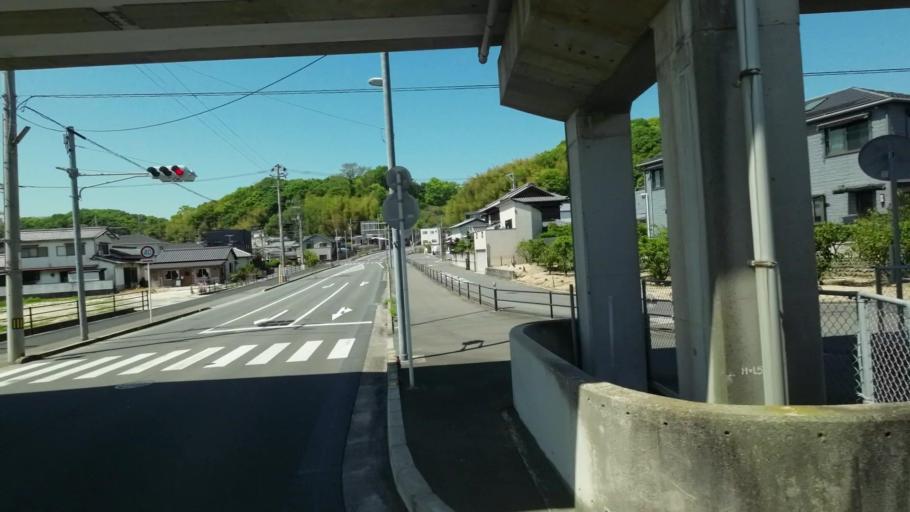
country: JP
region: Ehime
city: Hojo
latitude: 34.0711
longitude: 132.9875
